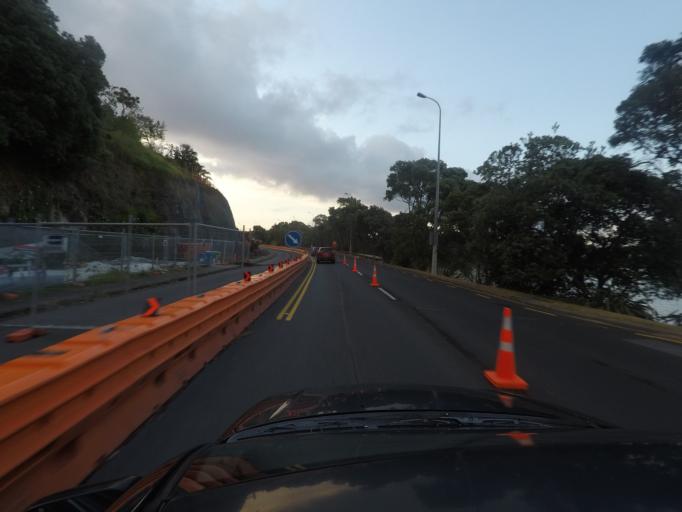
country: NZ
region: Auckland
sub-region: Auckland
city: Tamaki
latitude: -36.9036
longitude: 174.8547
